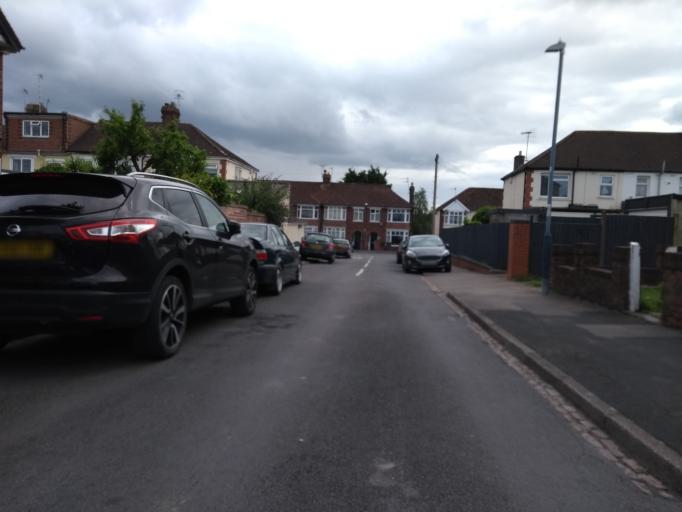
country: GB
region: England
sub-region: Warwickshire
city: Warwick
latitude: 52.2899
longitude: -1.5970
